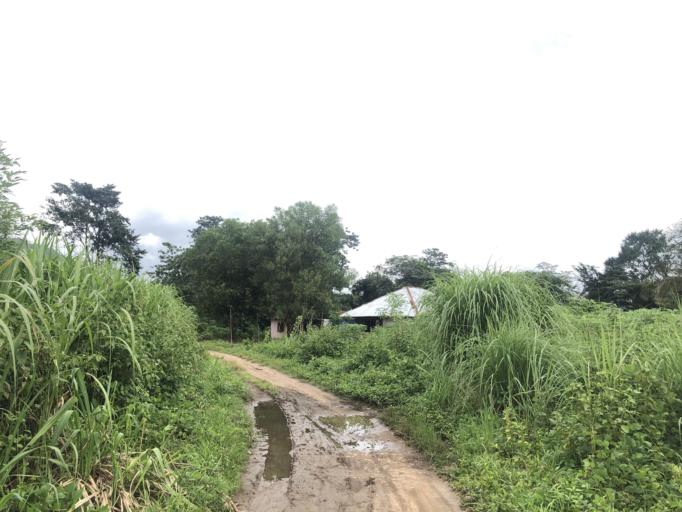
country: SL
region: Northern Province
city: Bumbuna
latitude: 8.9967
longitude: -11.7565
